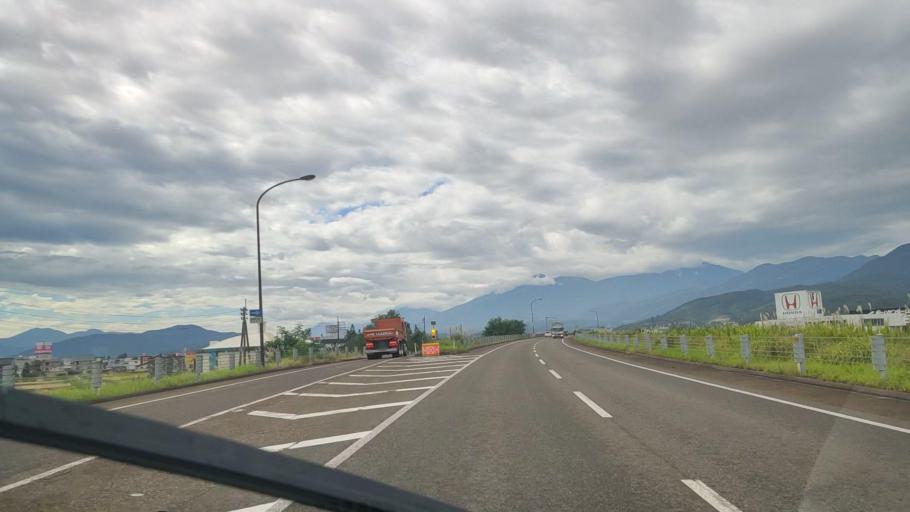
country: JP
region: Niigata
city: Arai
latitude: 37.0613
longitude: 138.2612
